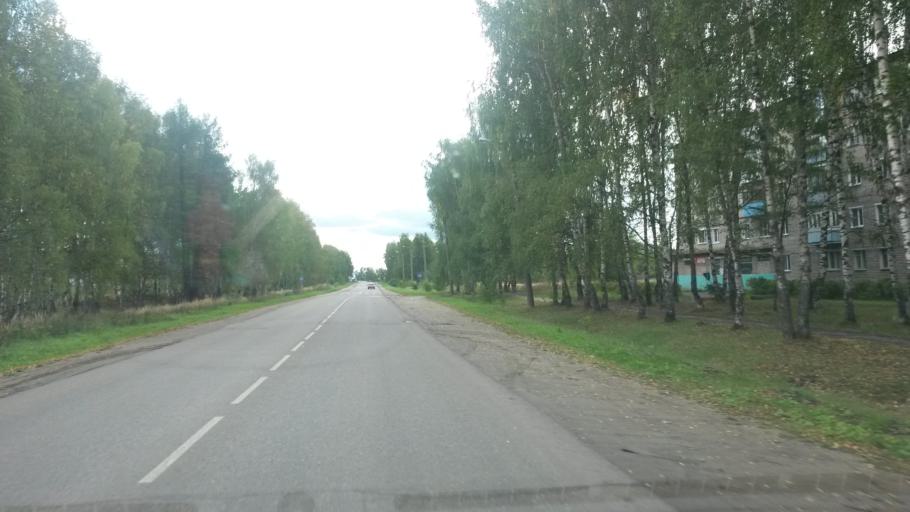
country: RU
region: Ivanovo
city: Zavolzhsk
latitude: 57.4711
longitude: 42.1587
